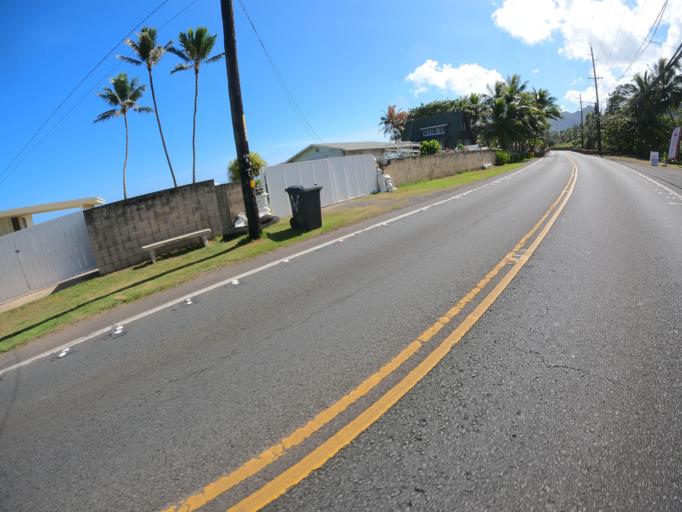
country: US
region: Hawaii
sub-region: Honolulu County
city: Hau'ula
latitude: 21.5986
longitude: -157.8973
